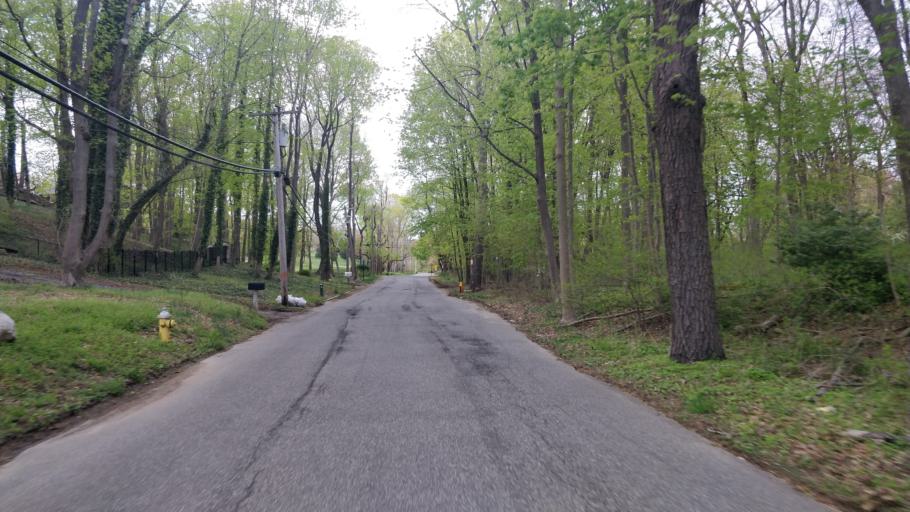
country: US
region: New York
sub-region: Suffolk County
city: Fort Salonga
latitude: 40.9153
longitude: -73.3009
